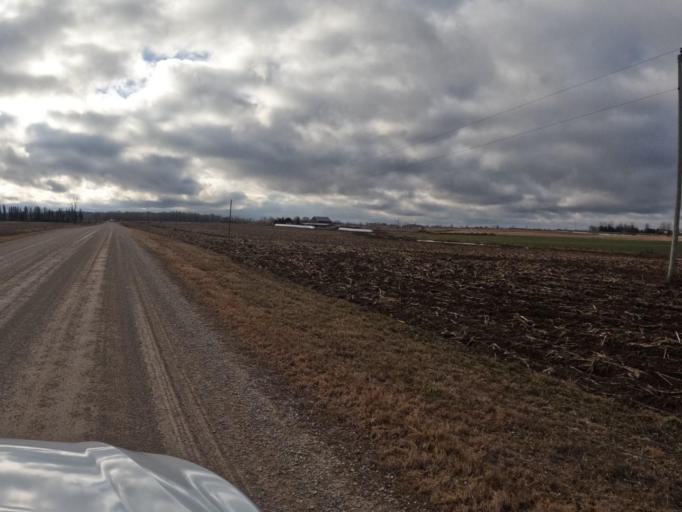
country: CA
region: Ontario
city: Shelburne
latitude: 43.8708
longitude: -80.3557
